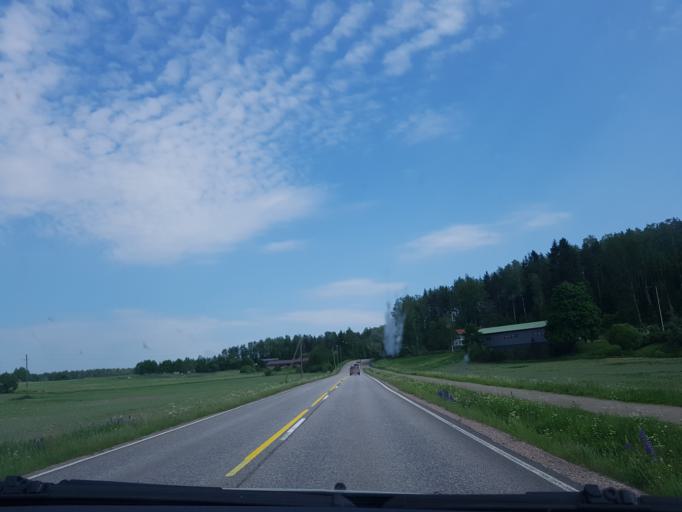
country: FI
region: Uusimaa
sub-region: Helsinki
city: Vihti
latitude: 60.3203
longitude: 24.4036
